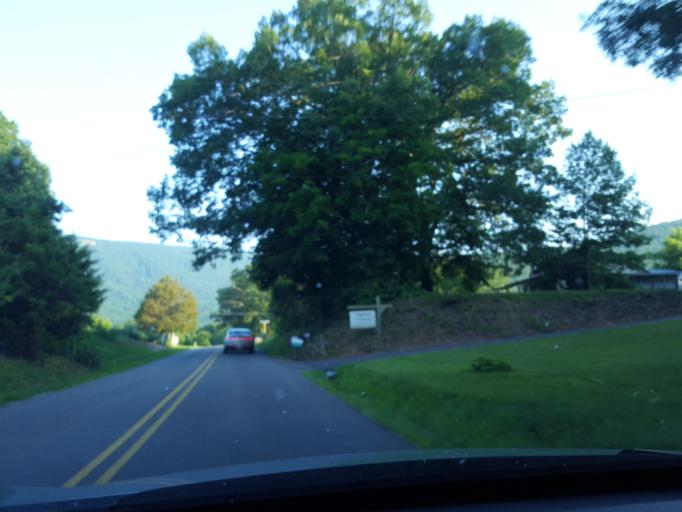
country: US
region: Virginia
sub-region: Augusta County
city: Lyndhurst
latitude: 37.9602
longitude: -78.9620
